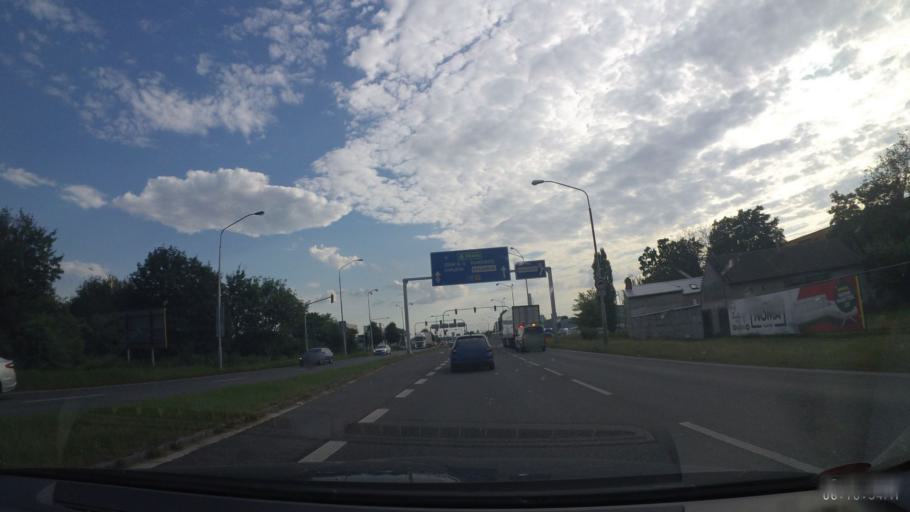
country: CZ
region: Kralovehradecky
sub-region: Okres Hradec Kralove
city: Hradec Kralove
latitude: 50.1971
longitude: 15.8149
